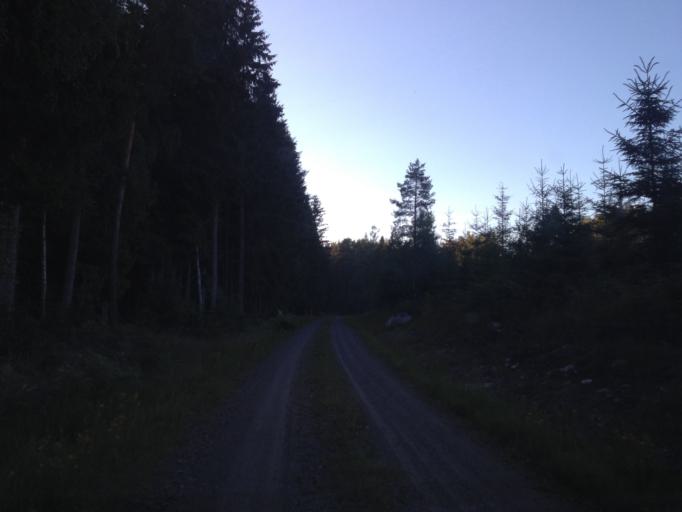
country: SE
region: Kalmar
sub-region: Vasterviks Kommun
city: Overum
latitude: 58.0035
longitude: 16.1220
